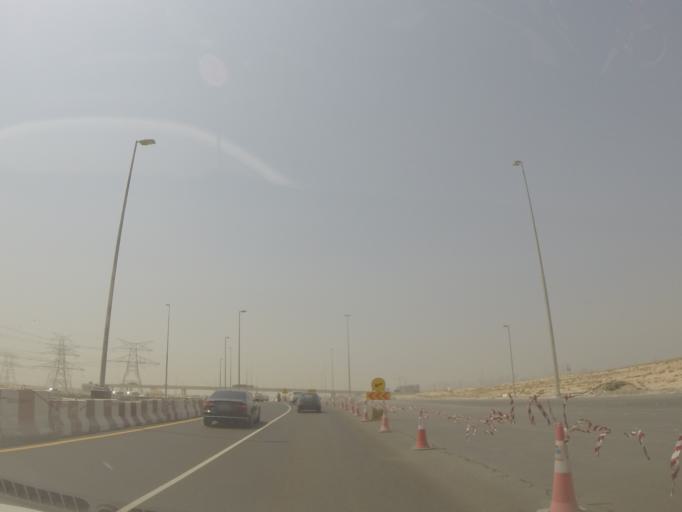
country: AE
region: Dubai
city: Dubai
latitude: 25.0131
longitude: 55.1648
